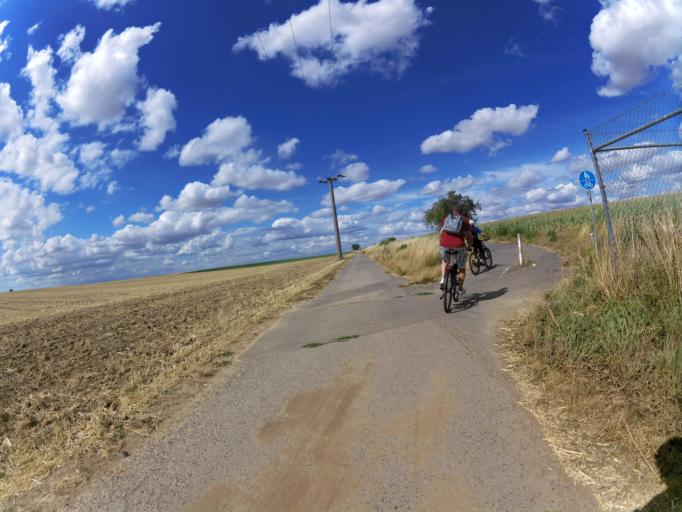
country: DE
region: Bavaria
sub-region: Regierungsbezirk Unterfranken
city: Sonderhofen
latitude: 49.5746
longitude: 10.0115
